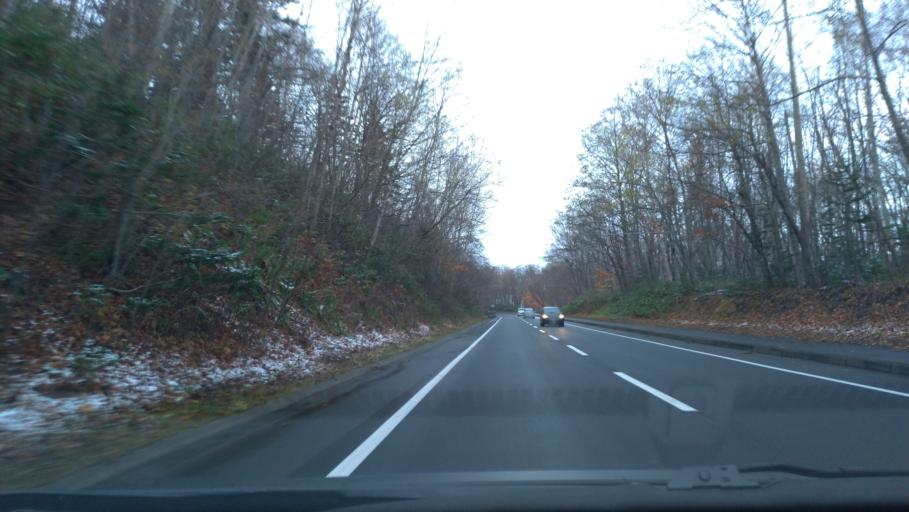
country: JP
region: Hokkaido
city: Shiraoi
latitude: 42.7363
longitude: 141.3616
